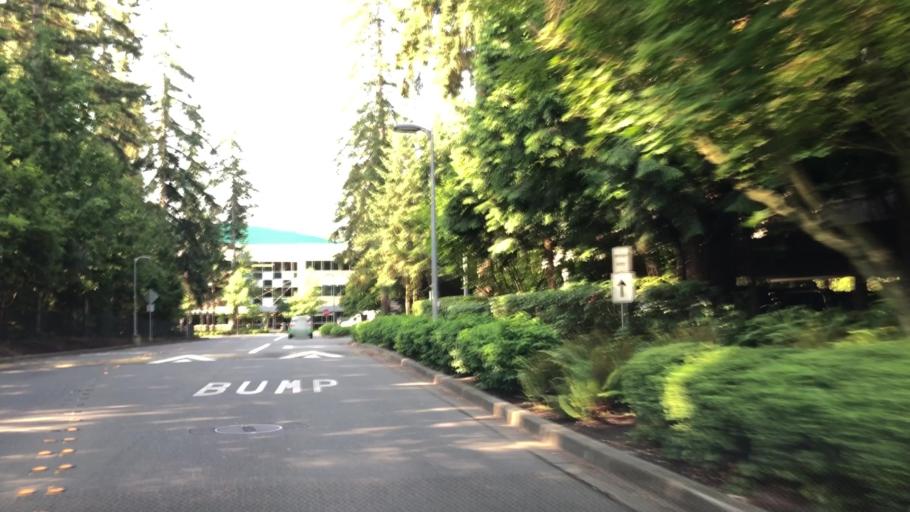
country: US
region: Washington
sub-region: King County
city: Redmond
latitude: 47.6417
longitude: -122.1369
